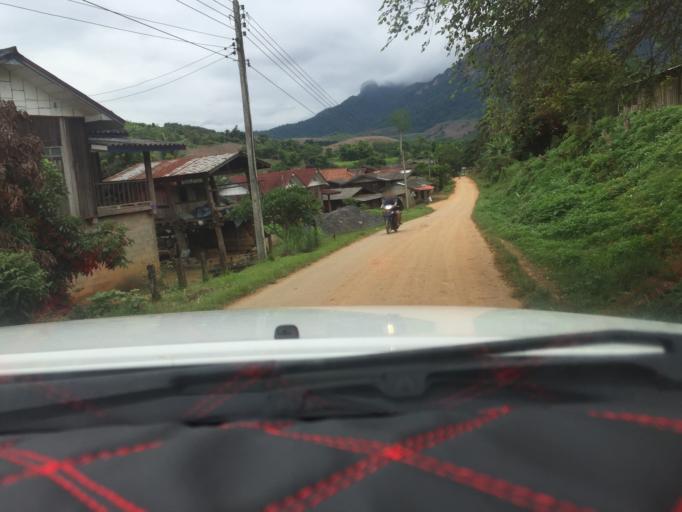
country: TH
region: Phayao
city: Phu Sang
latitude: 19.7650
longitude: 100.5092
